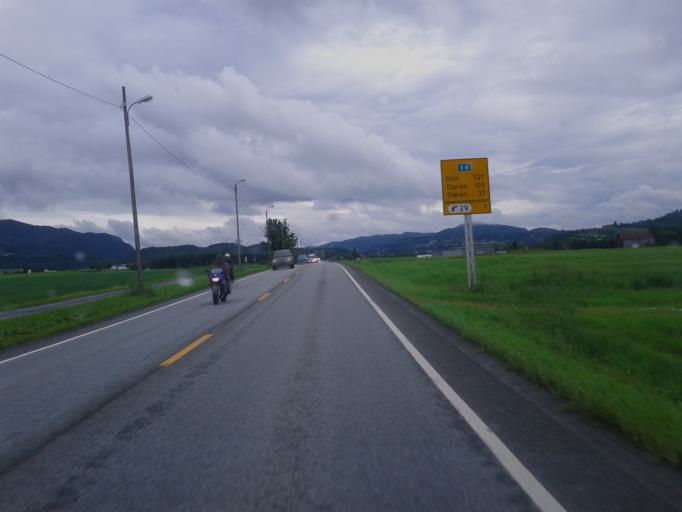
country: NO
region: Sor-Trondelag
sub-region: Melhus
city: Melhus
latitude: 63.3153
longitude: 10.2954
